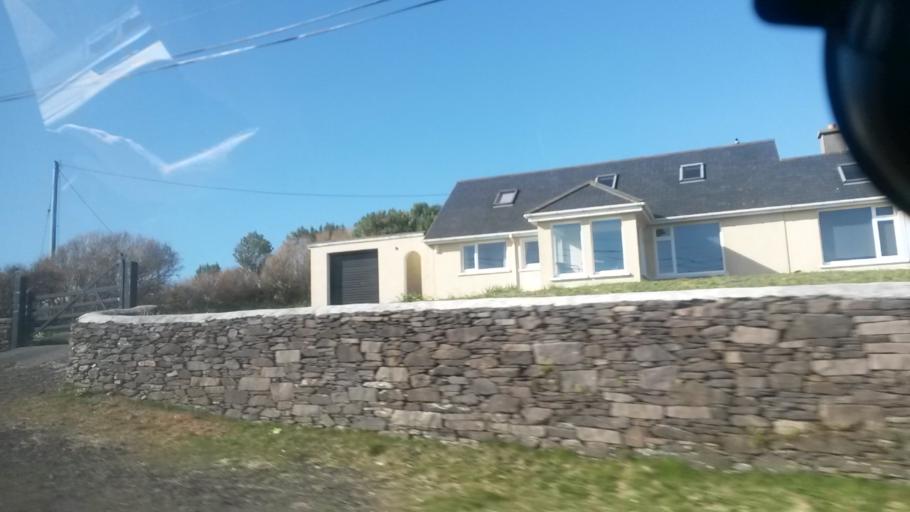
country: IE
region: Munster
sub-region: Ciarrai
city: Dingle
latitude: 52.1361
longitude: -10.4574
